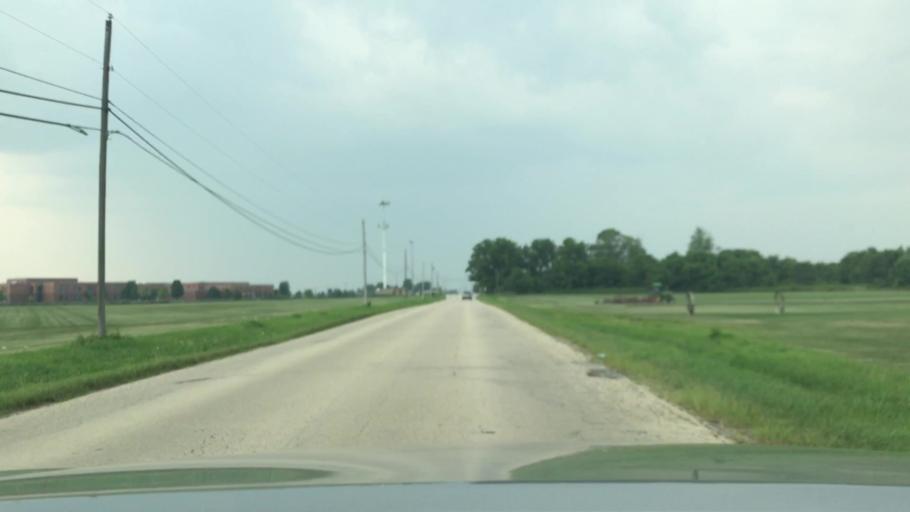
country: US
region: Illinois
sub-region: Will County
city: Plainfield
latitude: 41.6905
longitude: -88.2537
